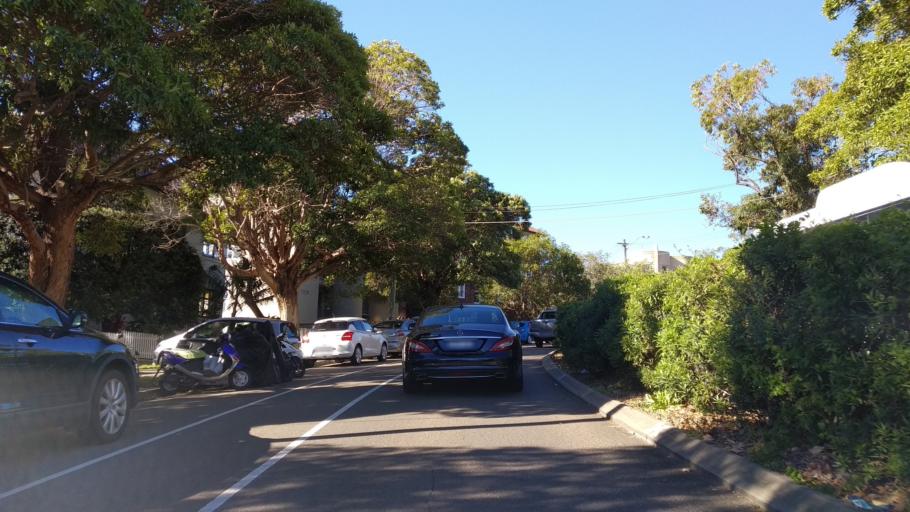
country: AU
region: New South Wales
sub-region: Waverley
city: Bondi Beach
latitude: -33.8855
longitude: 151.2652
